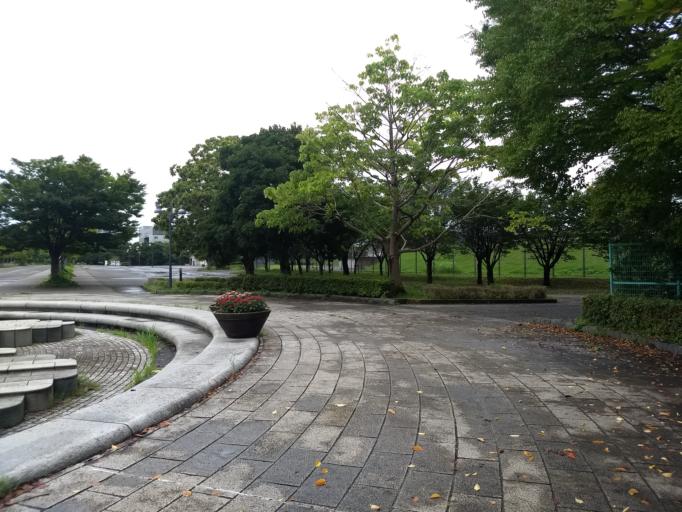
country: JP
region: Chiba
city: Kashiwa
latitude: 35.8973
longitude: 139.9381
